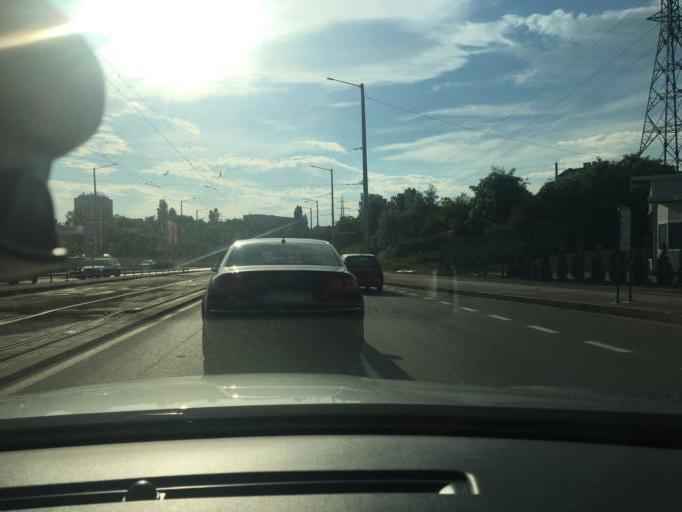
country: BG
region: Sofia-Capital
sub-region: Stolichna Obshtina
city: Sofia
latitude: 42.6751
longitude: 23.3758
